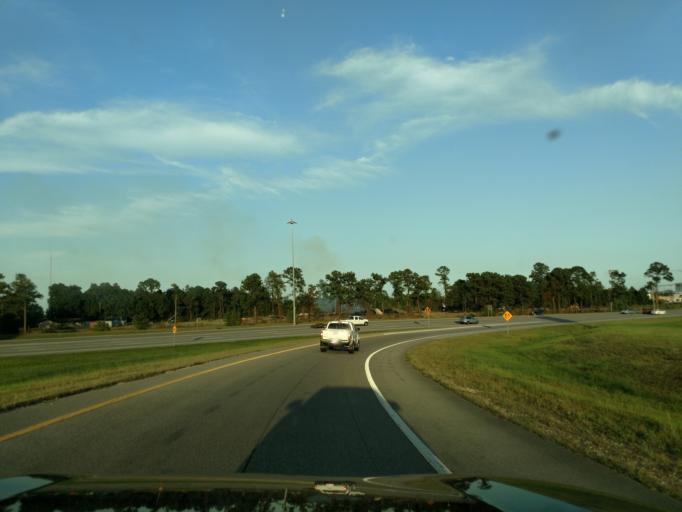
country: US
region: Mississippi
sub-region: Harrison County
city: West Gulfport
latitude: 30.4309
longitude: -89.0938
